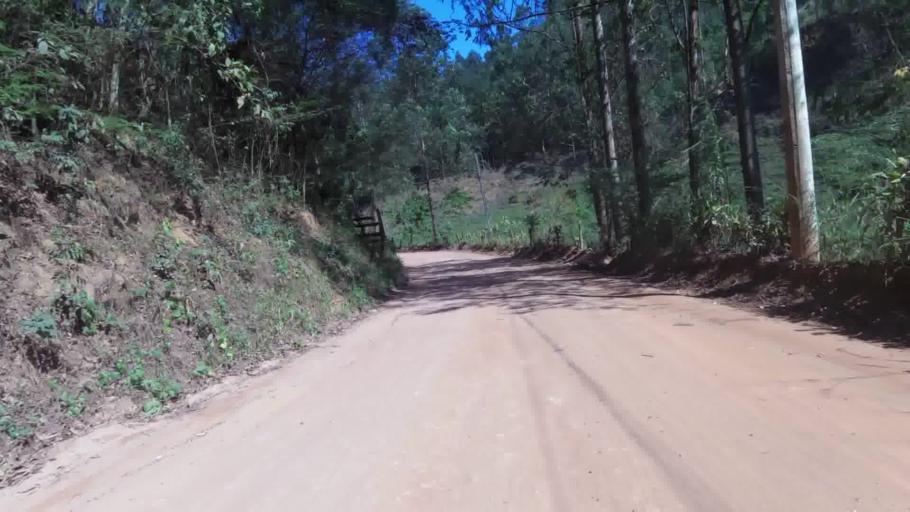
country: BR
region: Espirito Santo
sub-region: Alfredo Chaves
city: Alfredo Chaves
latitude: -20.6517
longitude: -40.8062
